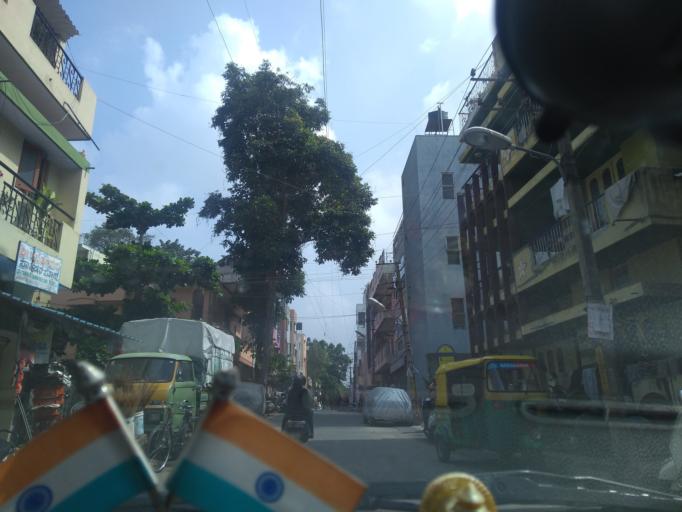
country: IN
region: Karnataka
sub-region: Bangalore Urban
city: Bangalore
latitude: 13.0002
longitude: 77.5550
